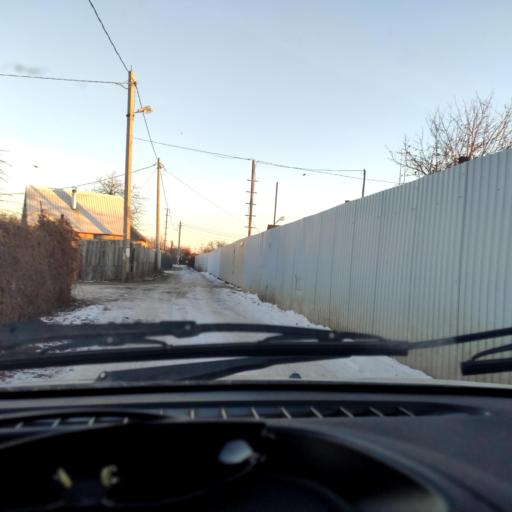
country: RU
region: Samara
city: Tol'yatti
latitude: 53.5419
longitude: 49.4316
